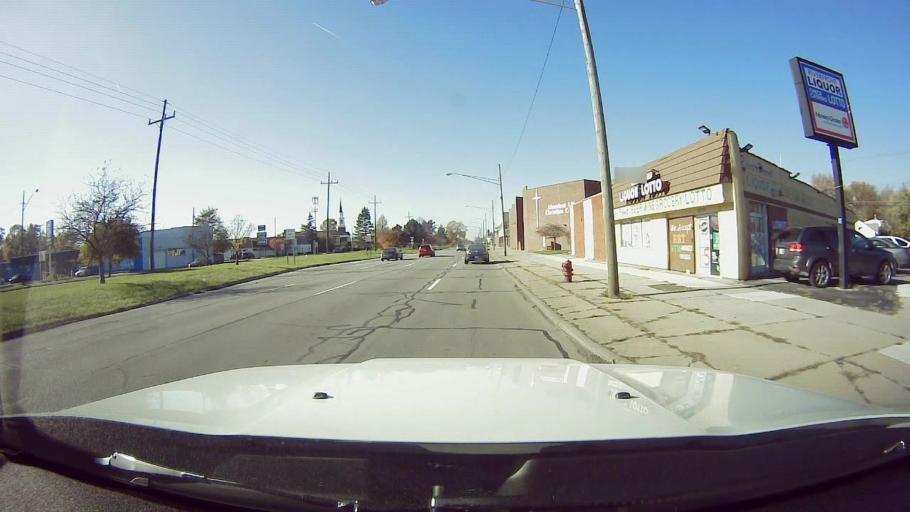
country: US
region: Michigan
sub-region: Wayne County
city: Redford
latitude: 42.4292
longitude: -83.2886
